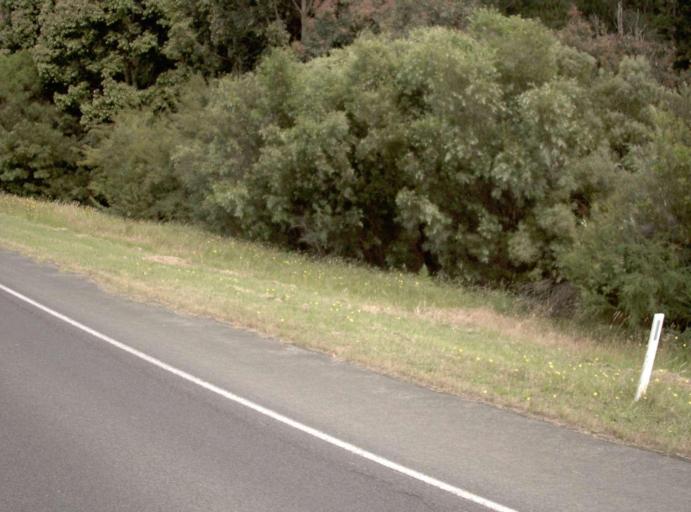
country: AU
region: Victoria
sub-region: Latrobe
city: Morwell
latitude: -38.1977
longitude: 146.4463
